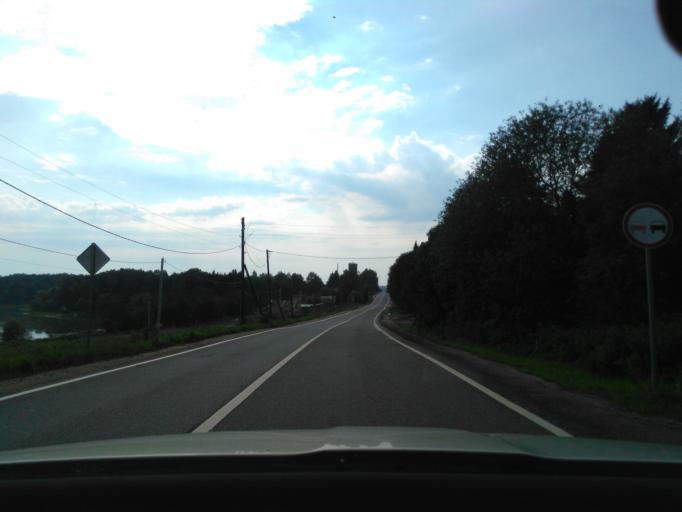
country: RU
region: Moskovskaya
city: Solnechnogorsk
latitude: 56.1424
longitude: 36.8747
